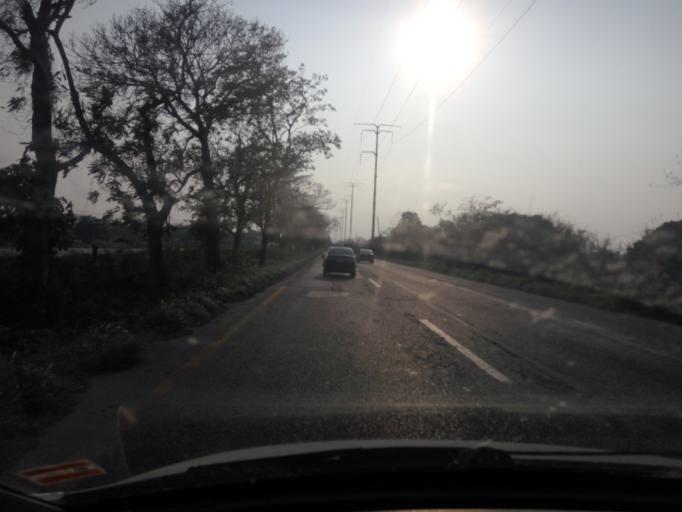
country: MX
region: Tabasco
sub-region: Centro
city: Anacleto Canabal 2da. Seccion
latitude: 17.9784
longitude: -93.0687
